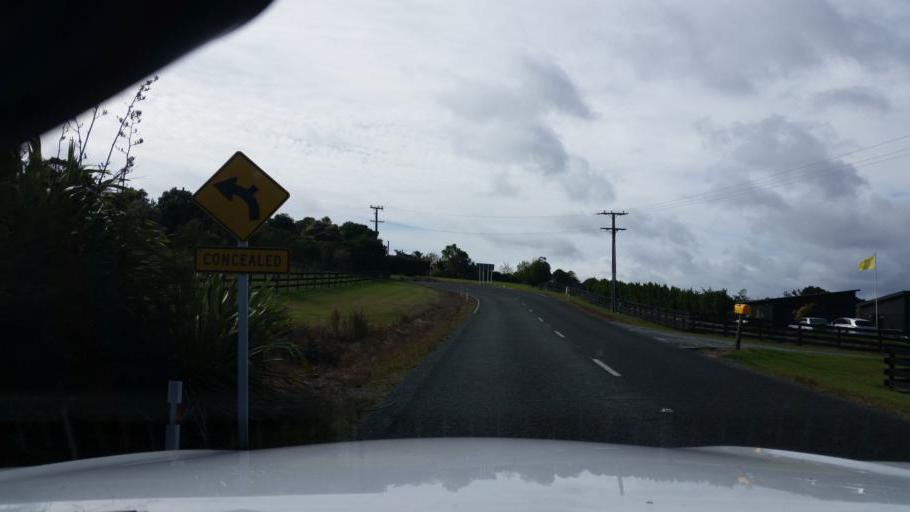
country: NZ
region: Auckland
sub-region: Auckland
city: Wellsford
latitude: -36.0901
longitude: 174.5313
